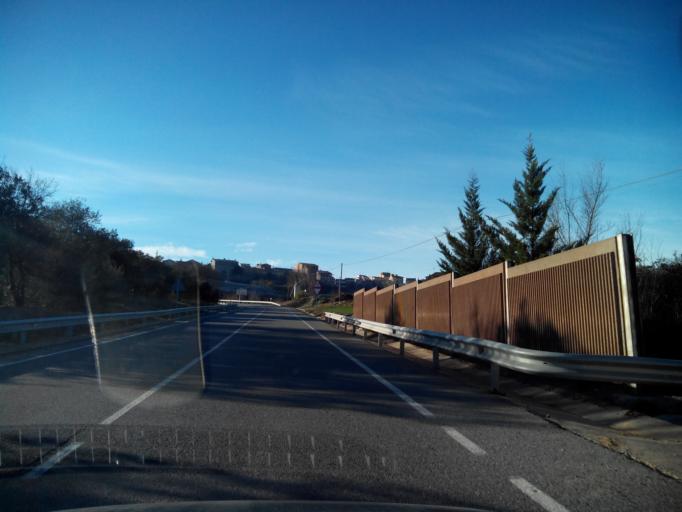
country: ES
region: Catalonia
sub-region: Provincia de Barcelona
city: Gironella
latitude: 42.0186
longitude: 1.8401
